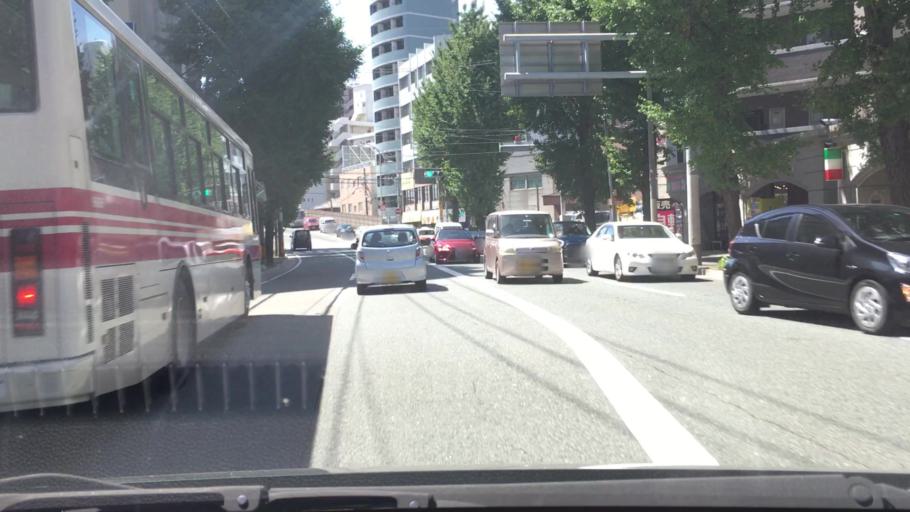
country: JP
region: Fukuoka
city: Fukuoka-shi
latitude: 33.5782
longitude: 130.4198
